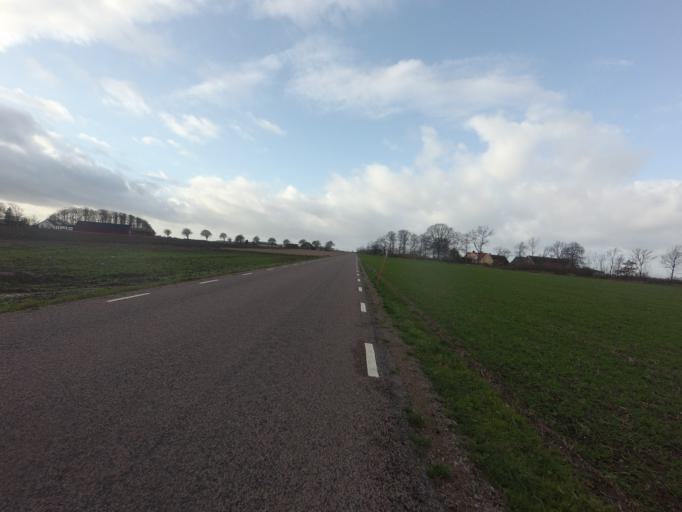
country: SE
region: Skane
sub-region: Hoganas Kommun
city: Hoganas
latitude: 56.1528
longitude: 12.6380
